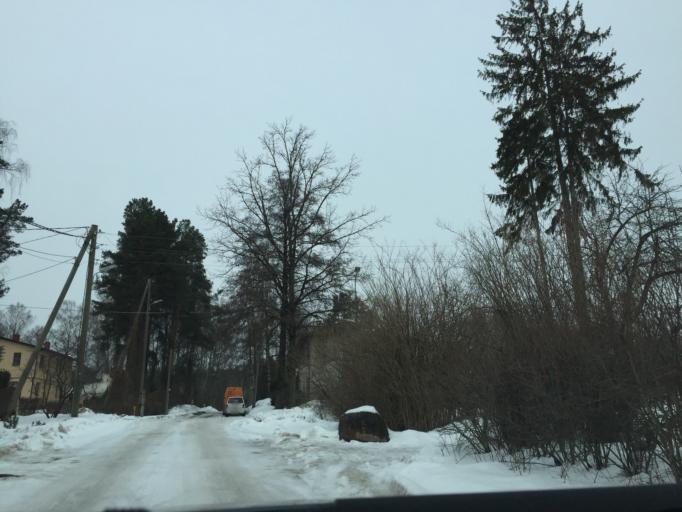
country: LV
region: Ogre
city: Ogre
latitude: 56.8212
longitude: 24.5751
